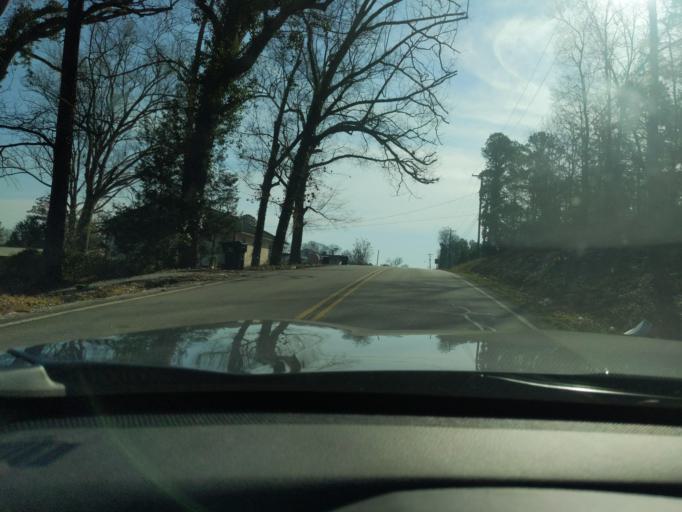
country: US
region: South Carolina
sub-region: Abbeville County
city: Calhoun Falls
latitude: 34.0893
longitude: -82.5916
